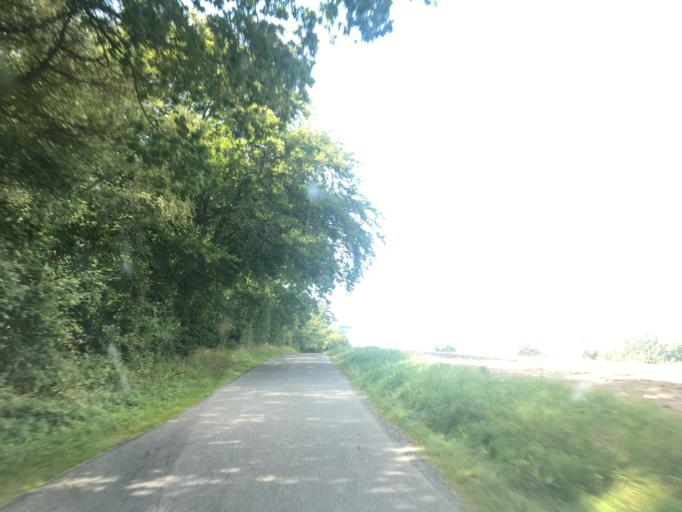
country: DK
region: South Denmark
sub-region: Middelfart Kommune
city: Ejby
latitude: 55.3930
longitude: 9.9267
